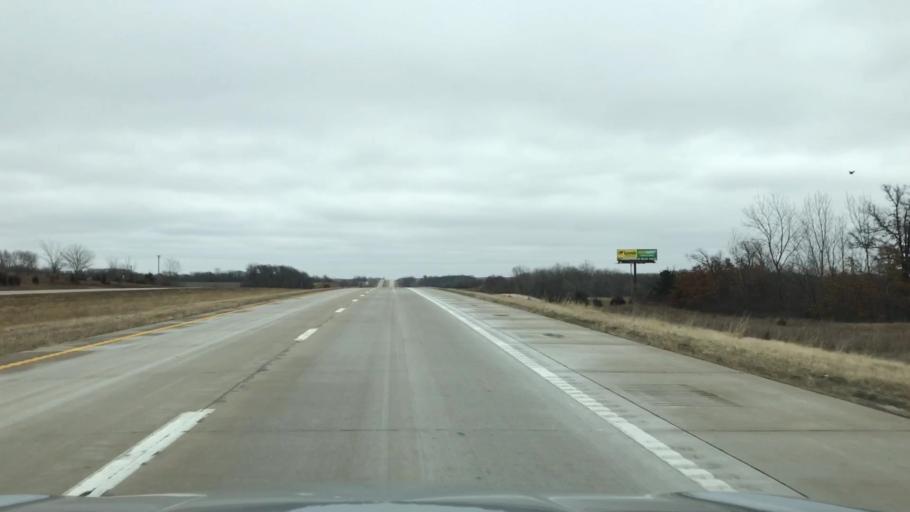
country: US
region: Missouri
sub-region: Livingston County
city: Chillicothe
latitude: 39.7356
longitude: -93.7442
